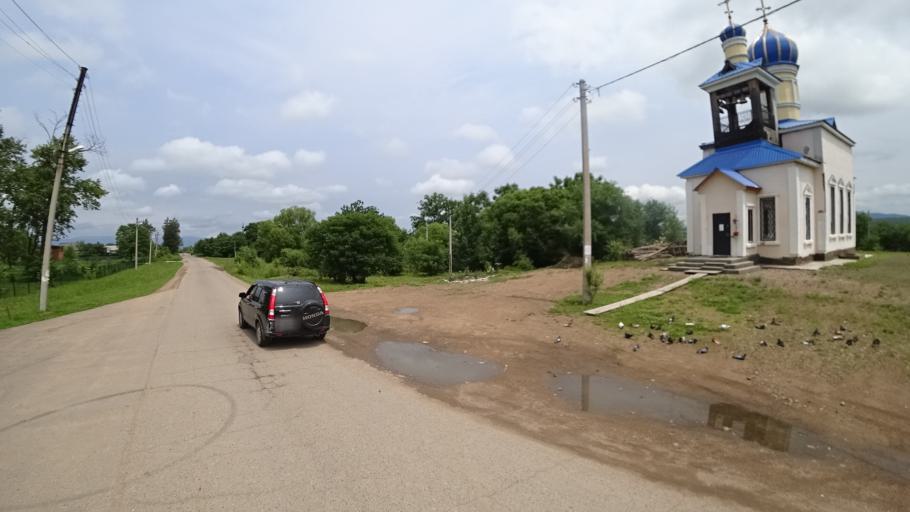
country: RU
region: Primorskiy
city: Novosysoyevka
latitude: 44.2295
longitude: 133.3610
